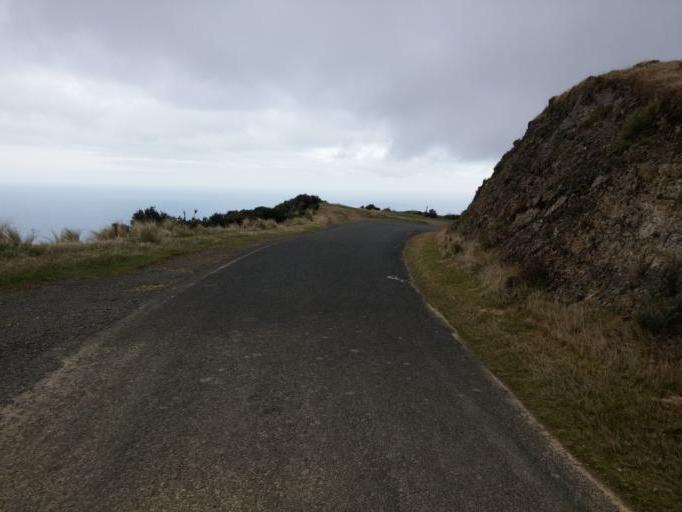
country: NZ
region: Wellington
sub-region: Wellington City
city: Brooklyn
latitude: -41.3259
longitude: 174.7322
